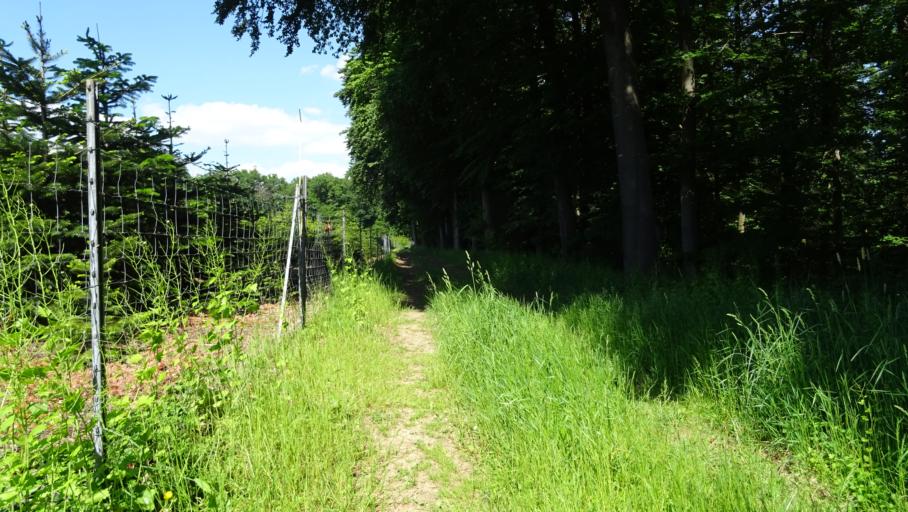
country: DE
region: Baden-Wuerttemberg
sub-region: Karlsruhe Region
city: Binau
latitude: 49.3803
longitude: 9.0619
